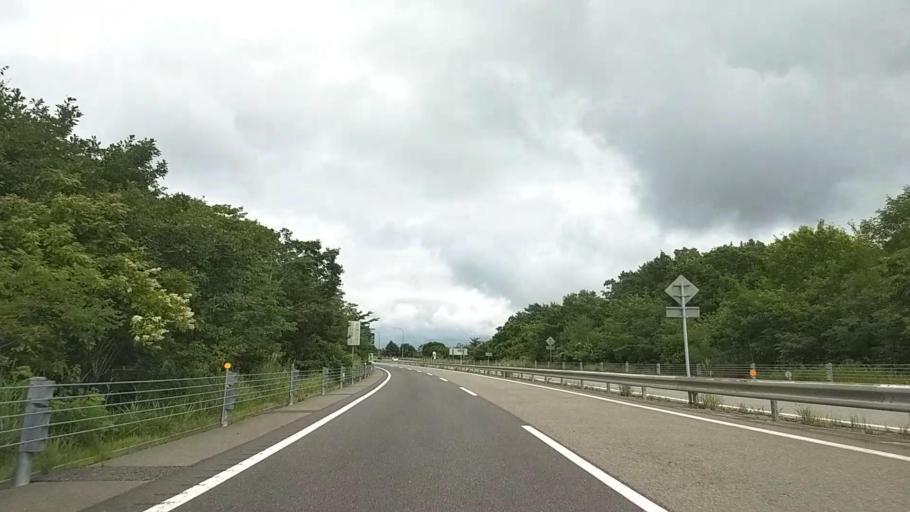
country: JP
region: Shizuoka
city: Gotemba
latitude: 35.4288
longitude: 138.8396
